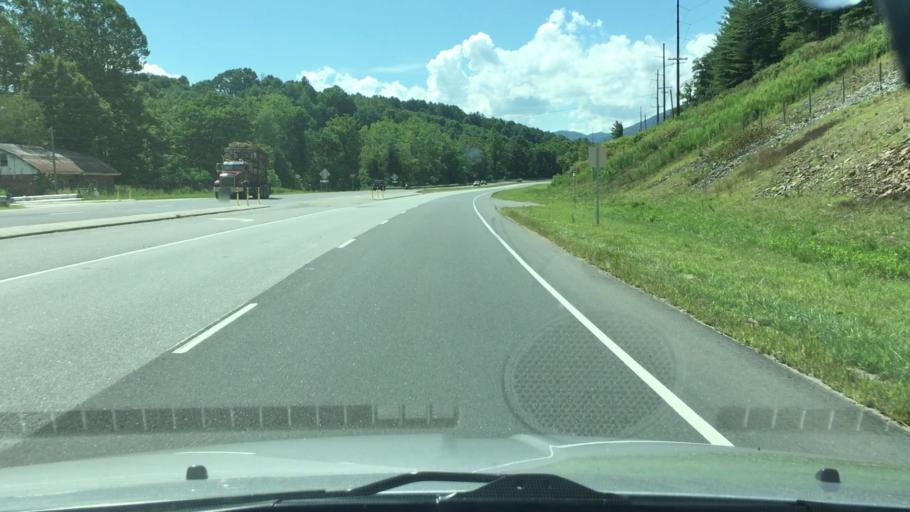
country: US
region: North Carolina
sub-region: Yancey County
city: Burnsville
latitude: 35.9110
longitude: -82.2304
